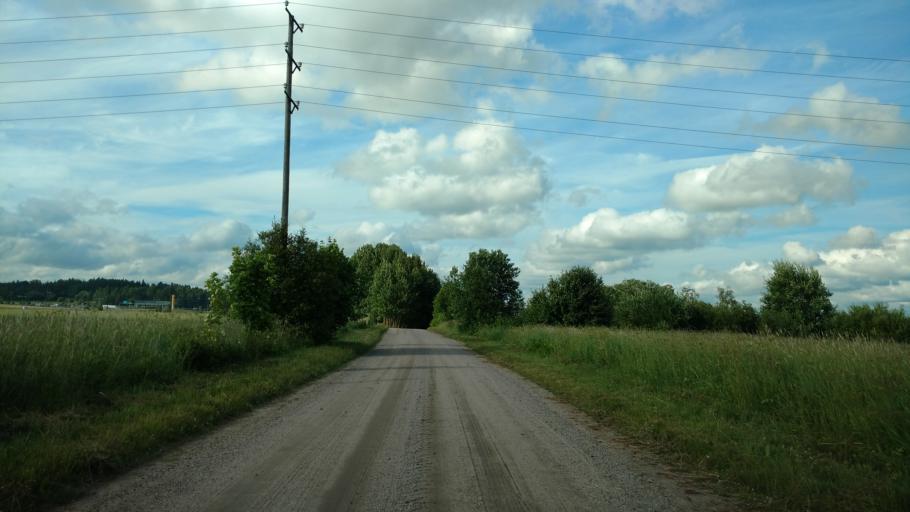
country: FI
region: Varsinais-Suomi
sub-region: Salo
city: Salo
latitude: 60.4093
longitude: 23.1656
